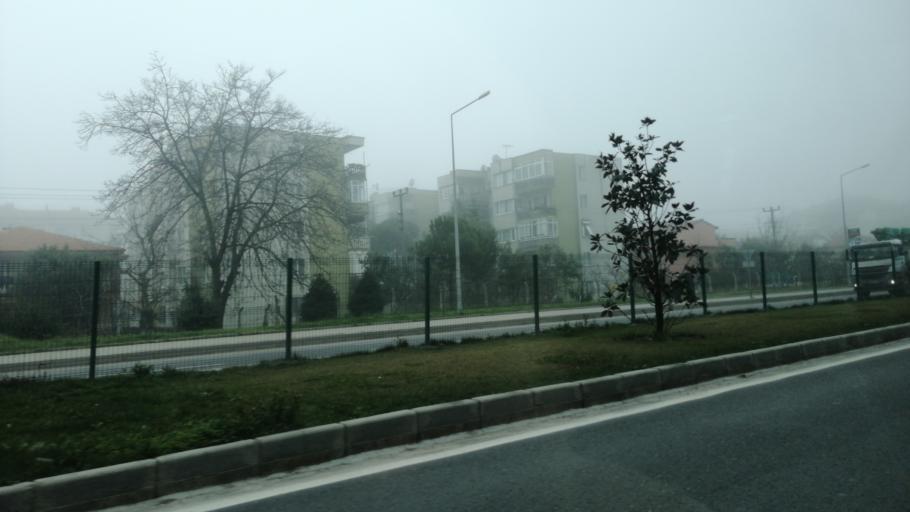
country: TR
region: Yalova
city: Yalova
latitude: 40.6579
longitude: 29.2892
